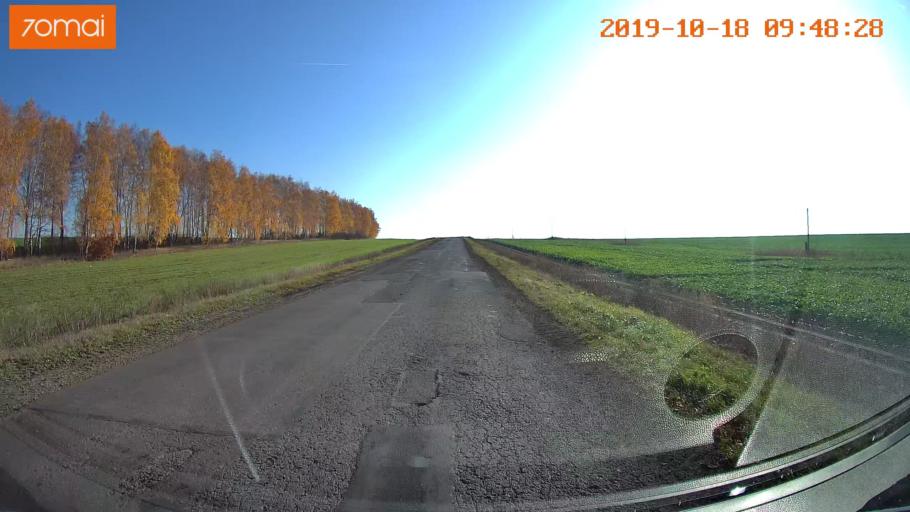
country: RU
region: Tula
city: Kazachka
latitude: 53.3178
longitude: 38.2500
